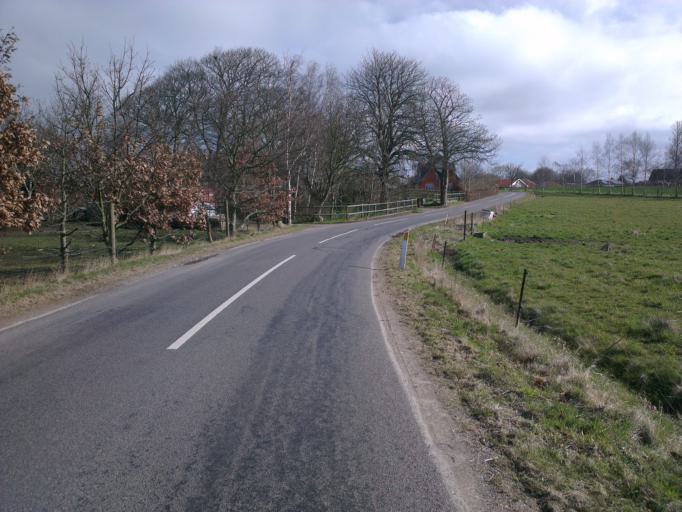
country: DK
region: Capital Region
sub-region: Hillerod Kommune
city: Skaevinge
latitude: 55.8814
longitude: 12.1252
